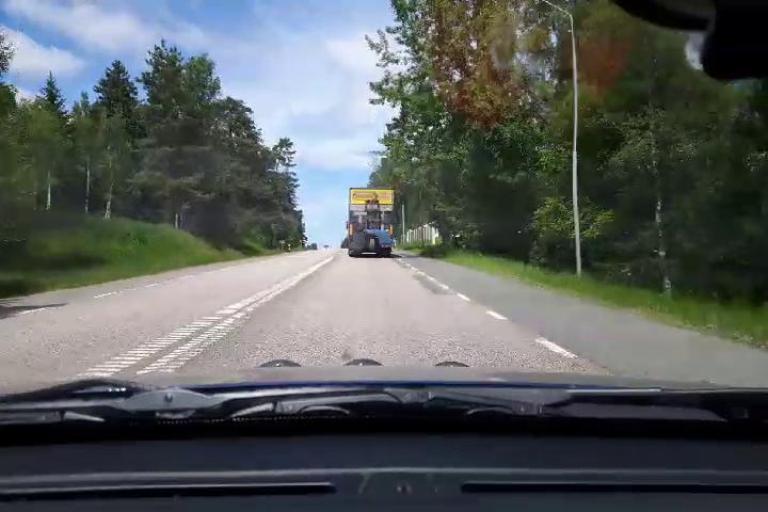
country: SE
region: Uppsala
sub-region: Osthammars Kommun
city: Bjorklinge
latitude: 60.0916
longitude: 17.5547
